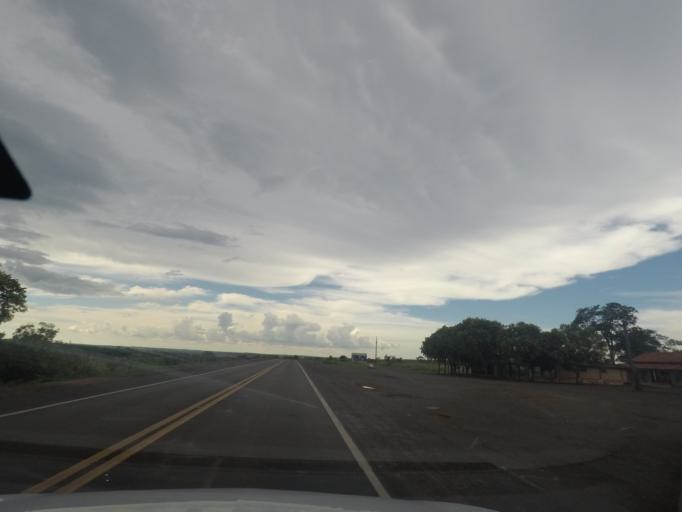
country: BR
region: Minas Gerais
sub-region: Prata
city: Prata
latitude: -19.5660
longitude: -48.8257
